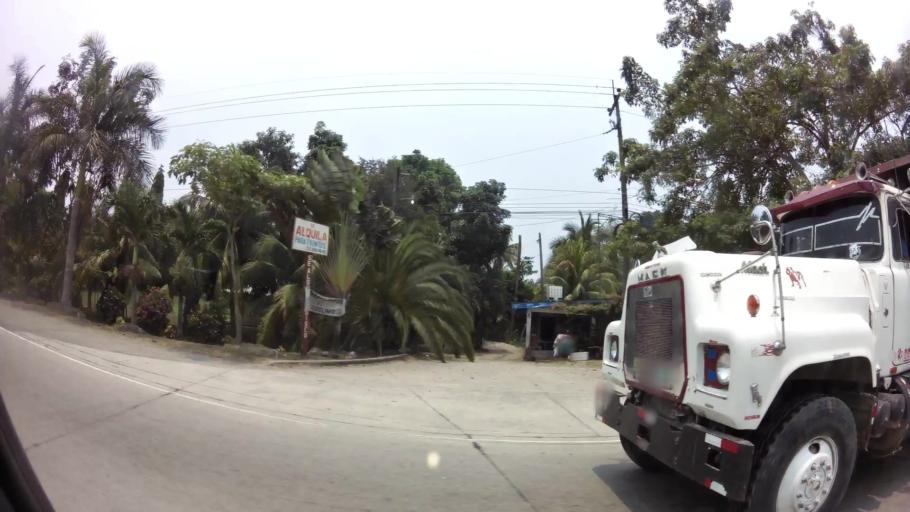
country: HN
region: Yoro
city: El Progreso
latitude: 15.4098
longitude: -87.8391
